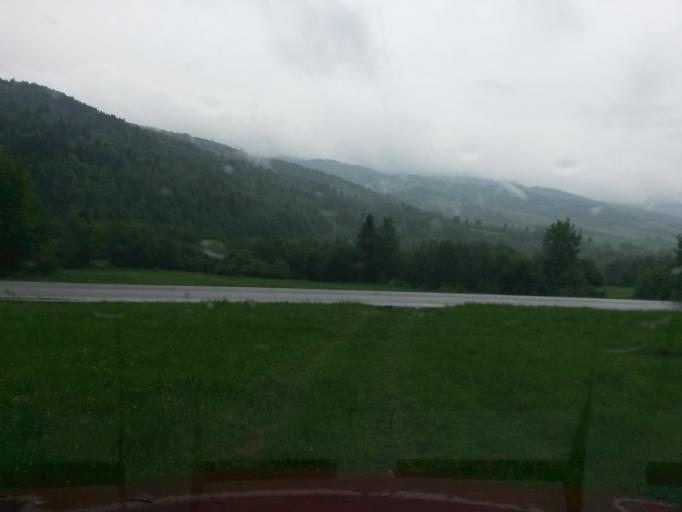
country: SK
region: Kosicky
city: Medzev
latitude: 48.7897
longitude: 20.7745
